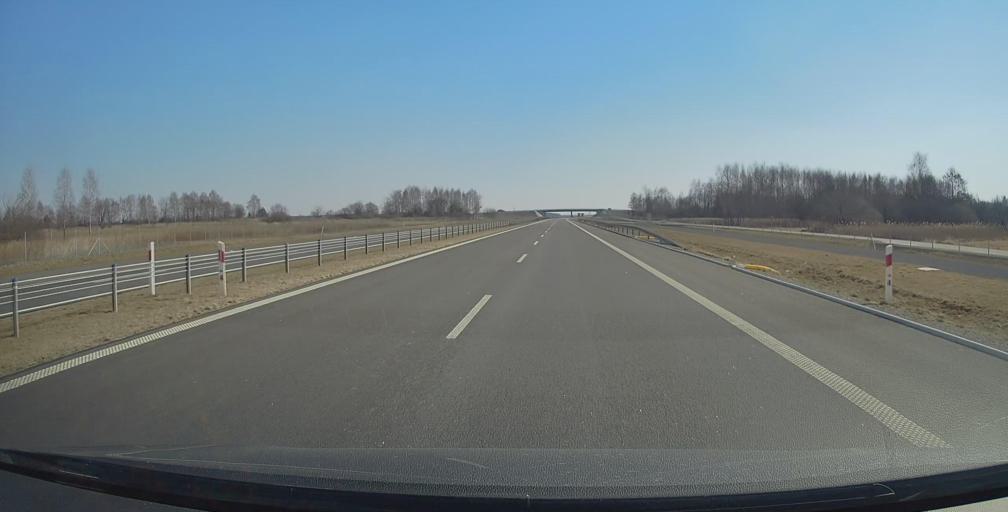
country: PL
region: Lublin Voivodeship
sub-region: Powiat janowski
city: Modliborzyce
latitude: 50.7387
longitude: 22.3298
